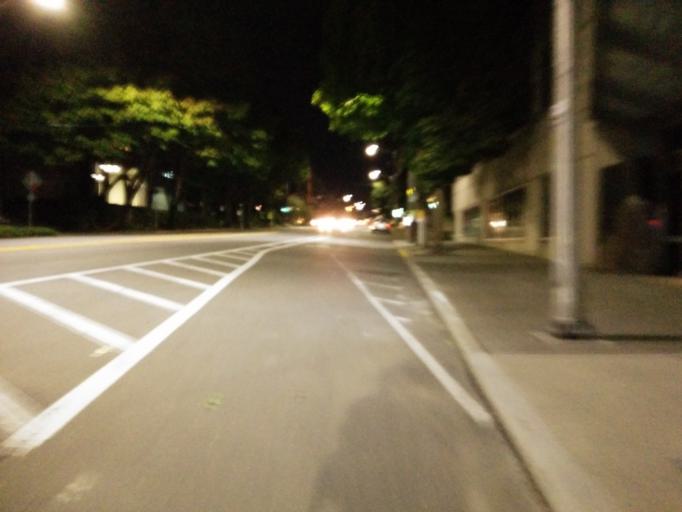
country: US
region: Washington
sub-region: King County
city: Seattle
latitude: 47.6326
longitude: -122.3422
